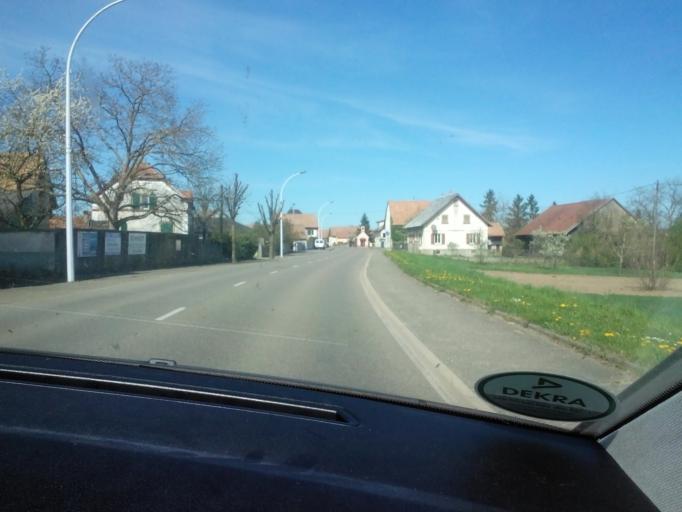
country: FR
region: Alsace
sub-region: Departement du Haut-Rhin
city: Fessenheim
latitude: 47.9252
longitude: 7.5367
